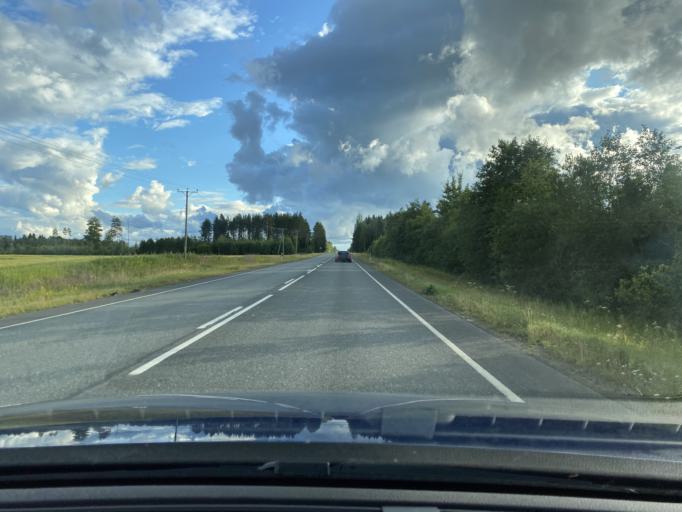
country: FI
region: Haeme
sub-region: Haemeenlinna
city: Renko
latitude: 60.8854
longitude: 24.2473
